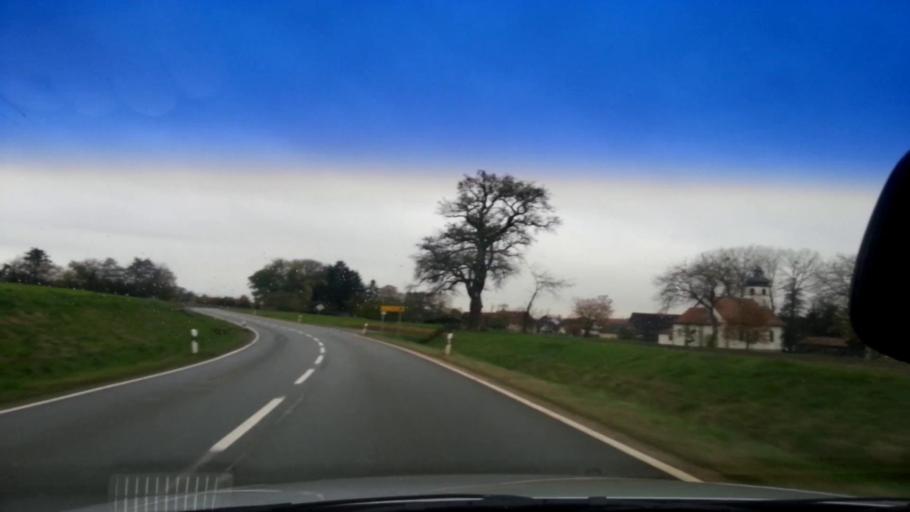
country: DE
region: Bavaria
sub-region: Upper Franconia
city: Schesslitz
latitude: 50.0004
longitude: 11.0604
